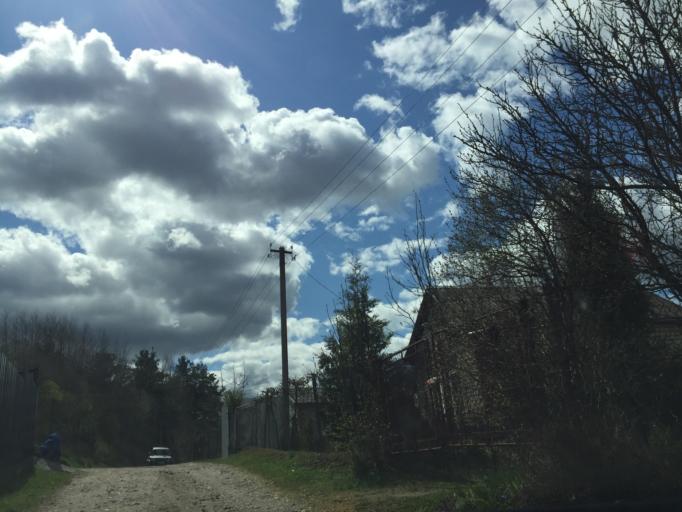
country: LV
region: Rezekne
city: Rezekne
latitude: 56.4857
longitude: 27.3264
